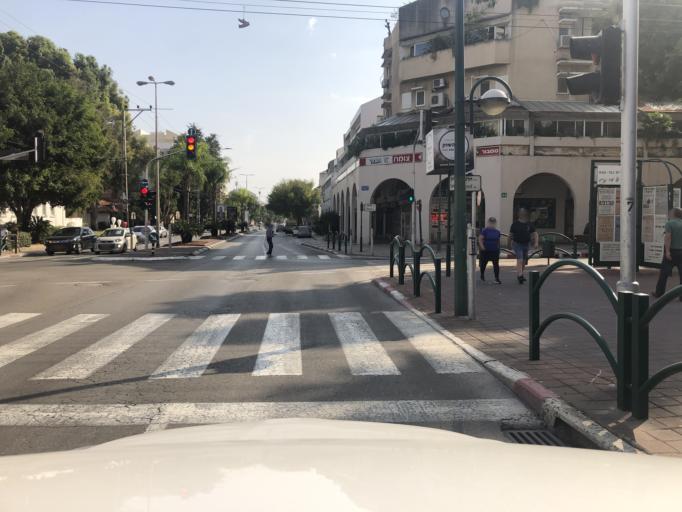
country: IL
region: Central District
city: Kfar Saba
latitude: 32.1747
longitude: 34.9109
